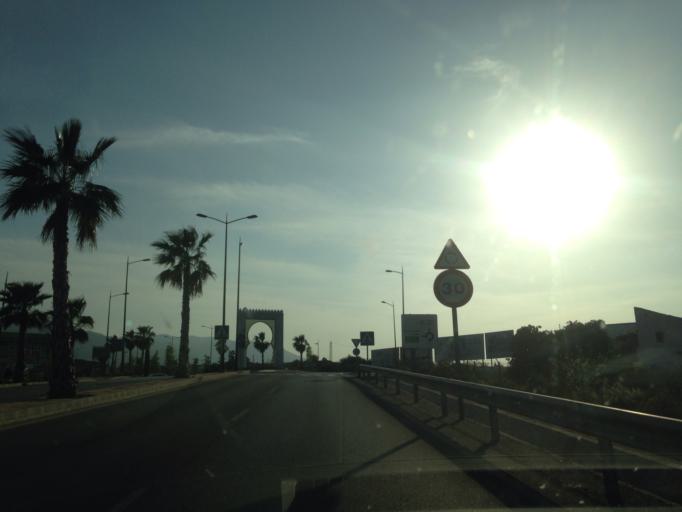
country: ES
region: Andalusia
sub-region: Provincia de Malaga
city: Alhaurin de la Torre
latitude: 36.6686
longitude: -4.5602
